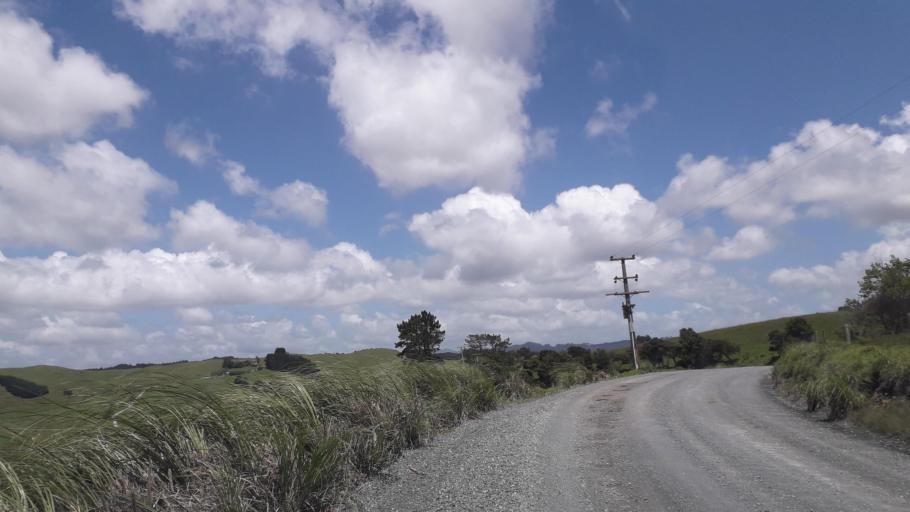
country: NZ
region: Northland
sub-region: Far North District
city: Taipa
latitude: -35.0013
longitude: 173.4314
